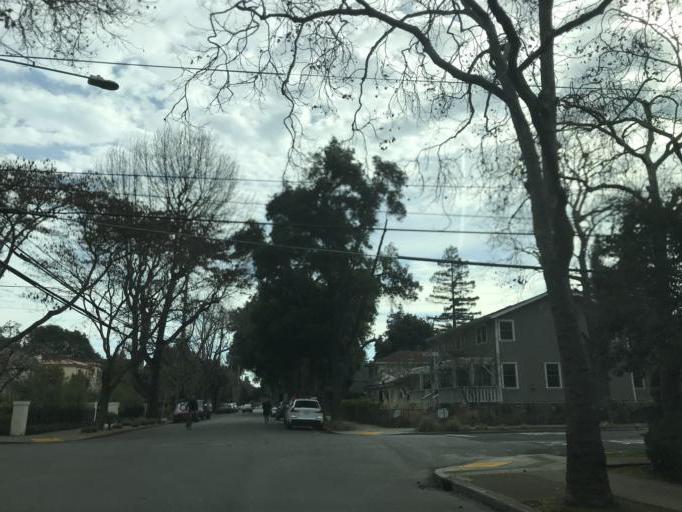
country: US
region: California
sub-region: Santa Clara County
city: Palo Alto
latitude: 37.4382
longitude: -122.1494
